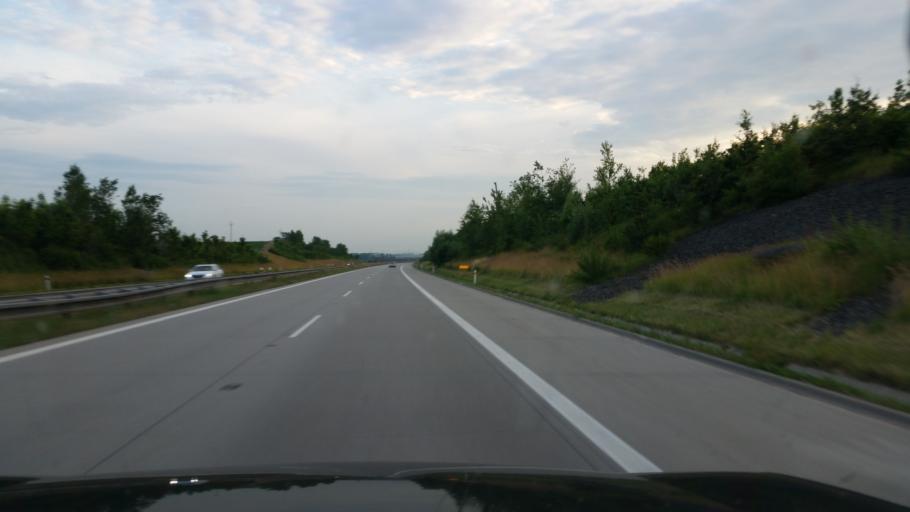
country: CZ
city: Bilovec
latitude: 49.7034
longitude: 17.9869
